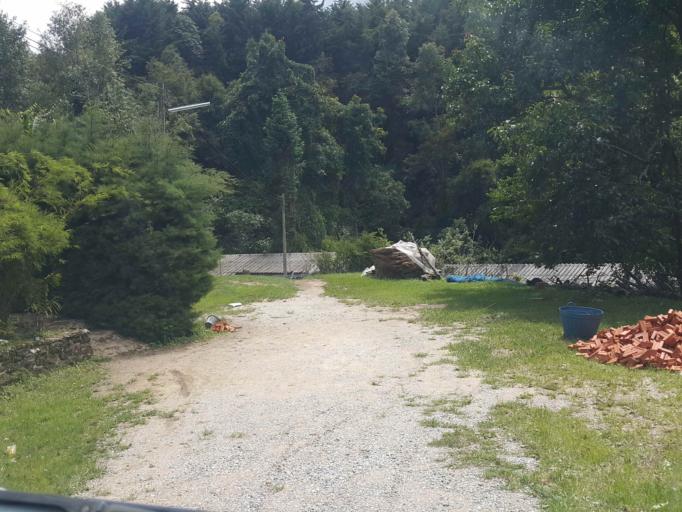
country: TH
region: Chiang Mai
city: Mae Chaem
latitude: 18.5181
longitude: 98.5297
